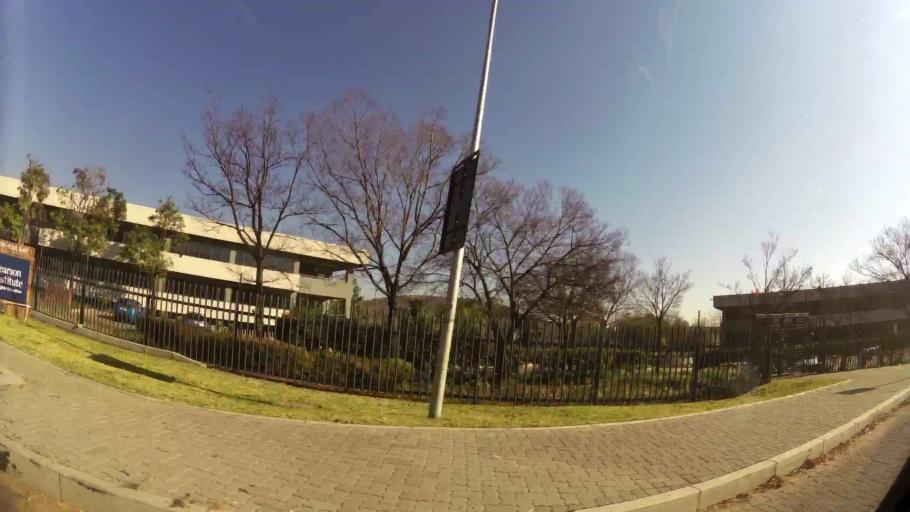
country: ZA
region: Gauteng
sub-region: Ekurhuleni Metropolitan Municipality
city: Germiston
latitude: -26.1723
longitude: 28.1342
